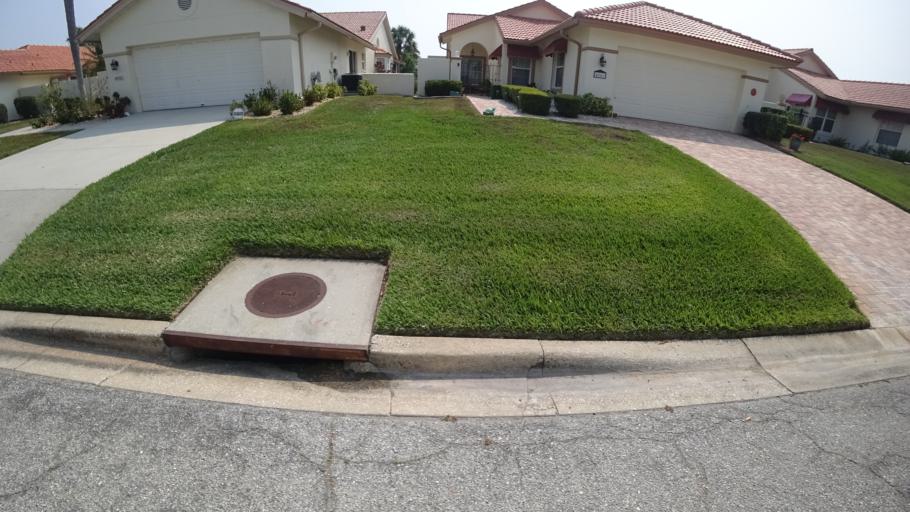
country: US
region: Florida
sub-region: Manatee County
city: Samoset
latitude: 27.4549
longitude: -82.5071
